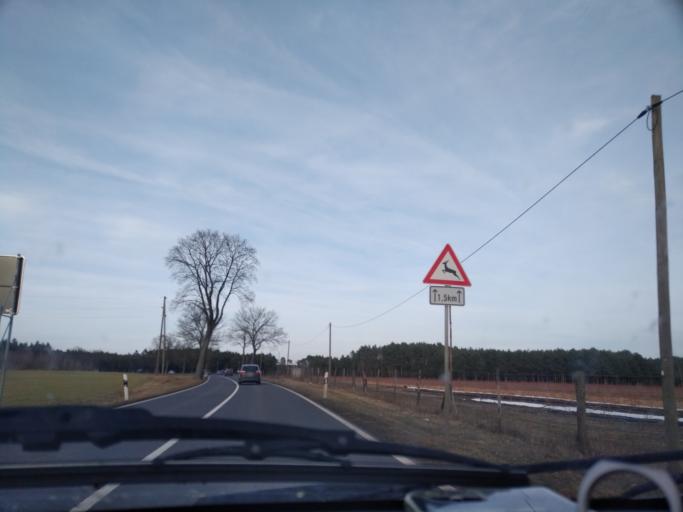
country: DE
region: Brandenburg
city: Luckenwalde
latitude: 52.1167
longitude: 13.2160
